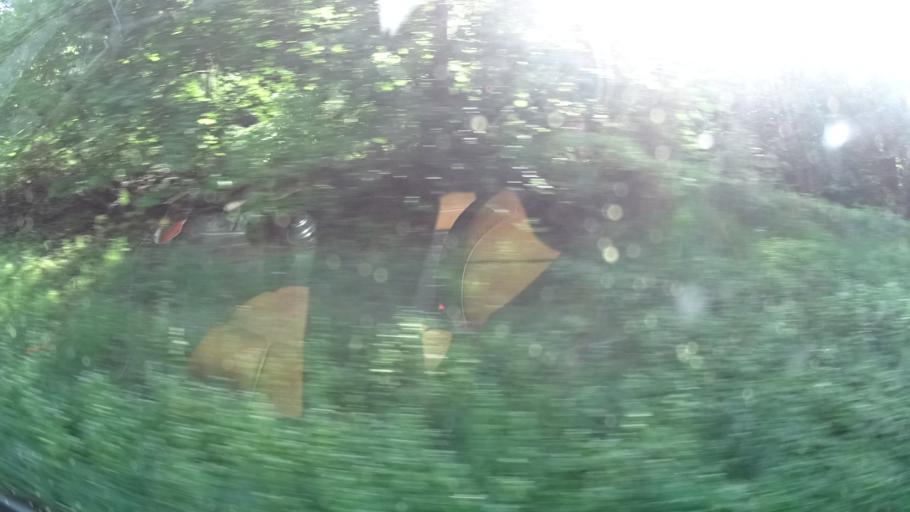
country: DE
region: Baden-Wuerttemberg
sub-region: Karlsruhe Region
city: Hofen an der Enz
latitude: 48.8087
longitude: 8.5842
